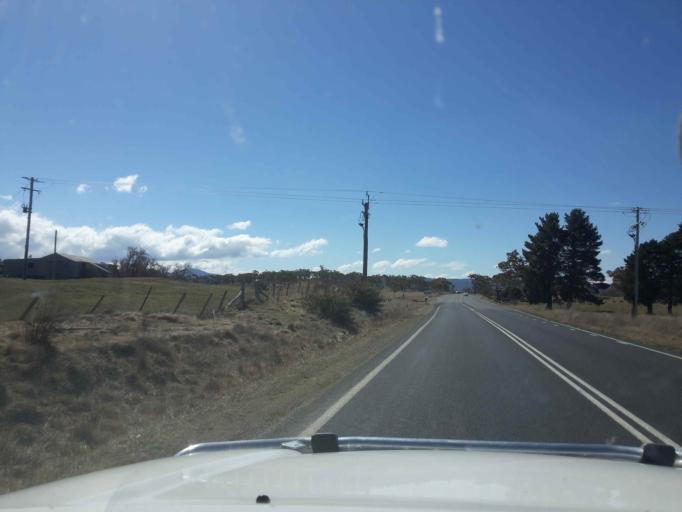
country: AU
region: New South Wales
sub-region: Snowy River
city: Jindabyne
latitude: -36.4340
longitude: 148.6078
